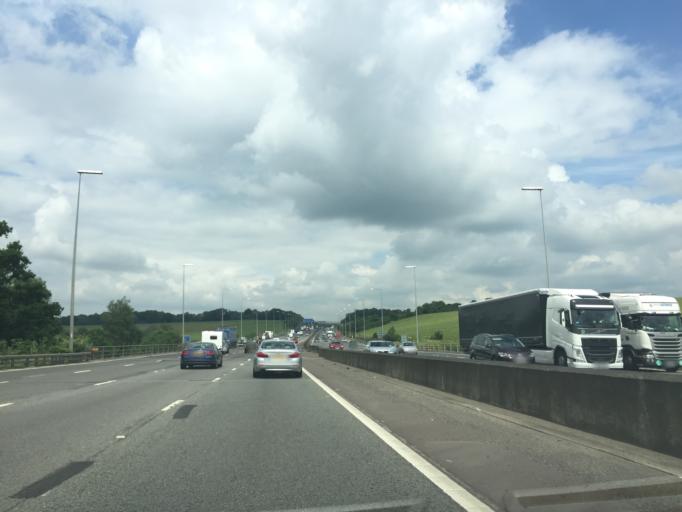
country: GB
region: England
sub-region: Buckinghamshire
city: Chalfont Saint Peter
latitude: 51.6266
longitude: -0.5223
